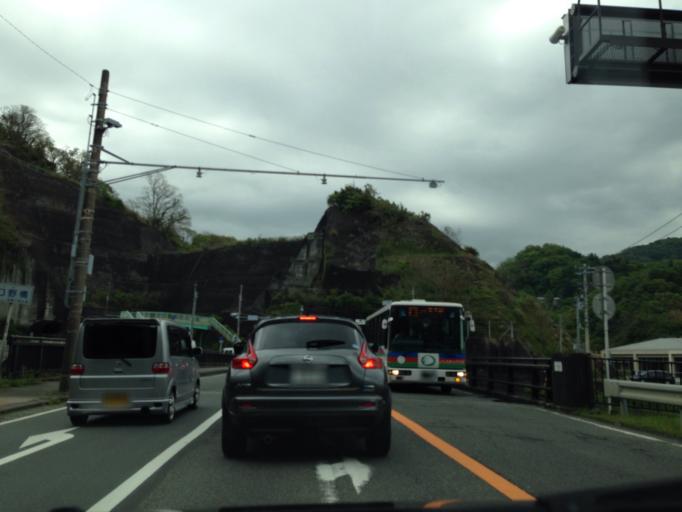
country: JP
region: Shizuoka
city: Numazu
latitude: 35.0487
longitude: 138.9061
